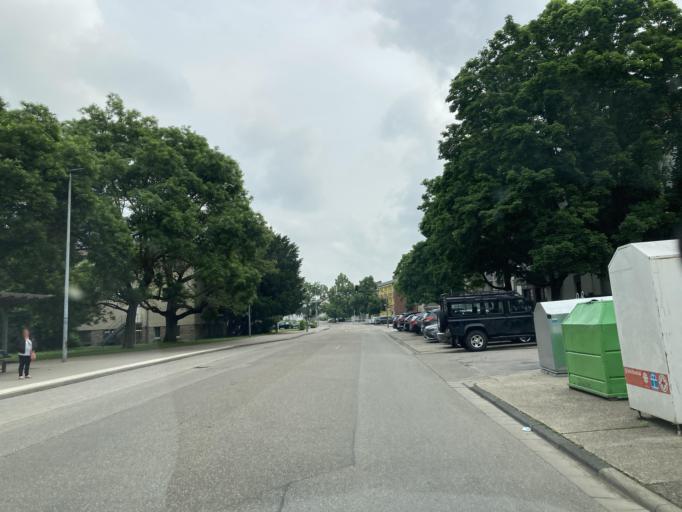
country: DE
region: Baden-Wuerttemberg
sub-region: Karlsruhe Region
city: Bruchsal
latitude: 49.1235
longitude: 8.5831
